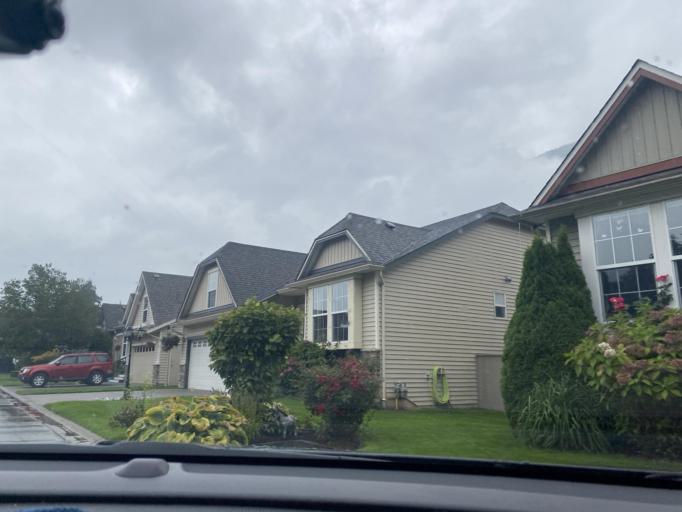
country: CA
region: British Columbia
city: Agassiz
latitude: 49.2990
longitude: -121.7818
